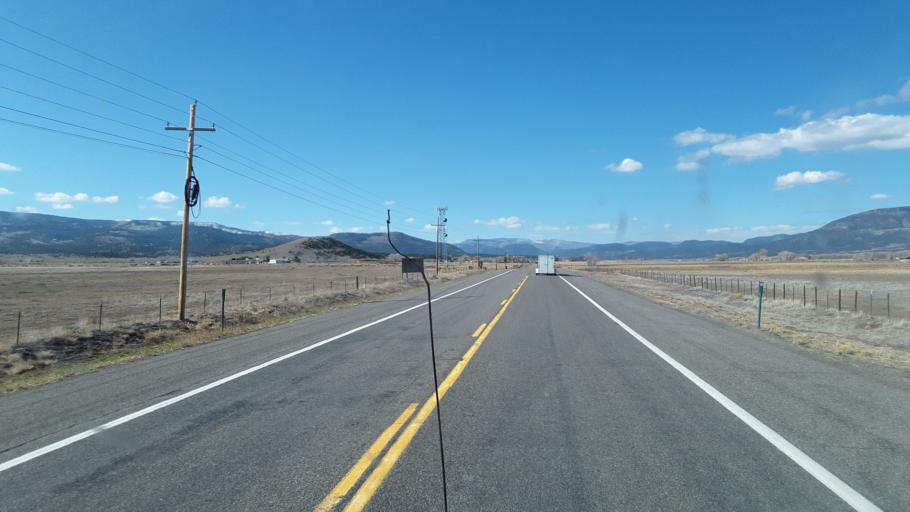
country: US
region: Colorado
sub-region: Rio Grande County
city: Del Norte
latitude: 37.6768
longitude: -106.4519
